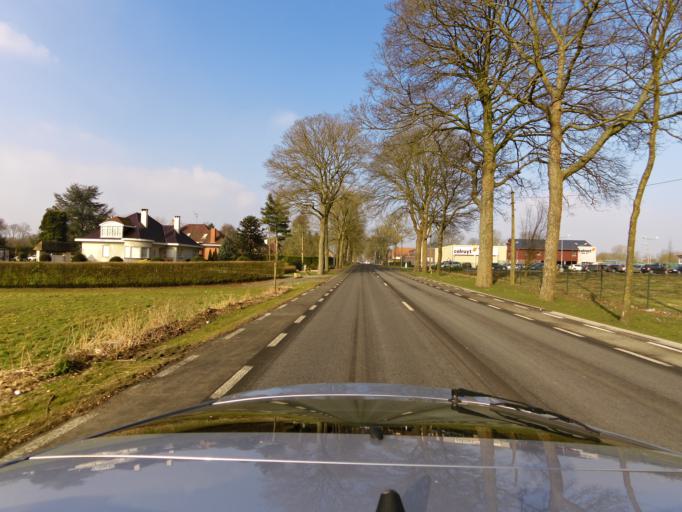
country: BE
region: Wallonia
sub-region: Province du Hainaut
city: Bernissart
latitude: 50.5109
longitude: 3.6820
